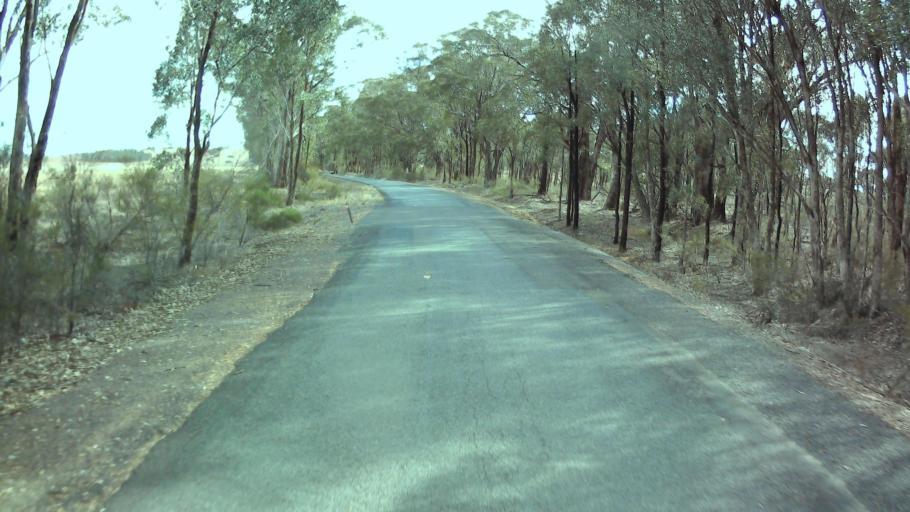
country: AU
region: New South Wales
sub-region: Weddin
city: Grenfell
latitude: -33.8476
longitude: 148.2342
